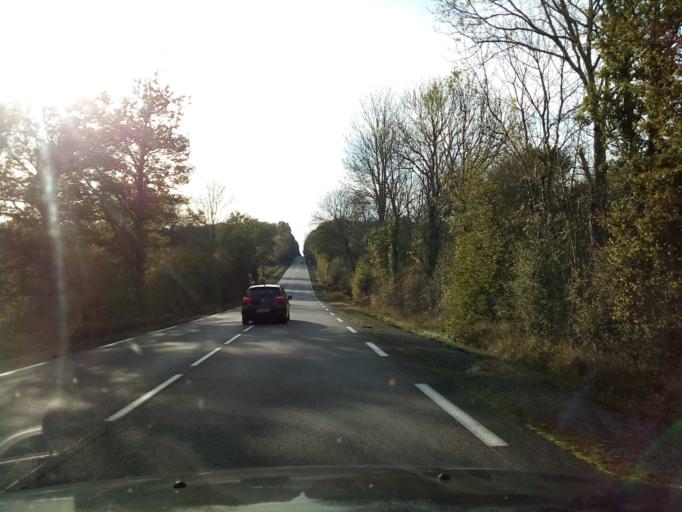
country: FR
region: Limousin
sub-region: Departement de la Haute-Vienne
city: Peyrat-de-Bellac
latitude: 46.1180
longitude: 0.9499
